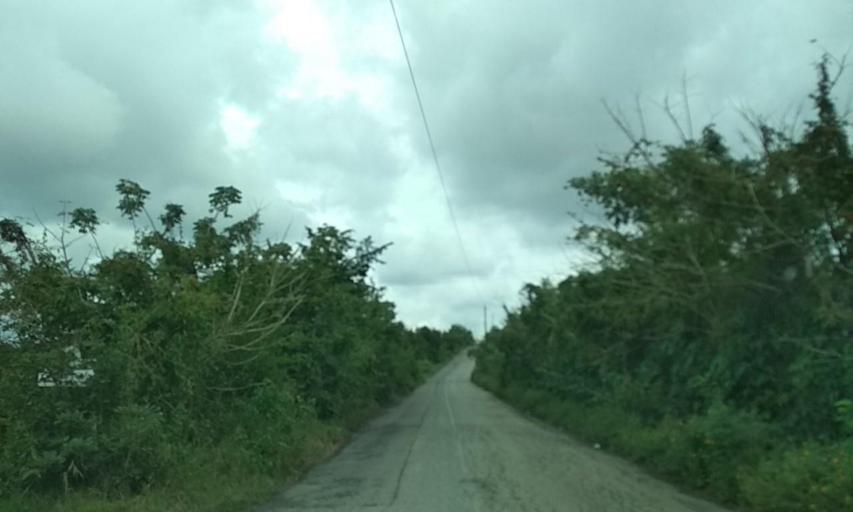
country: MX
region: Puebla
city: Espinal
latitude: 20.3276
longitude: -97.4134
